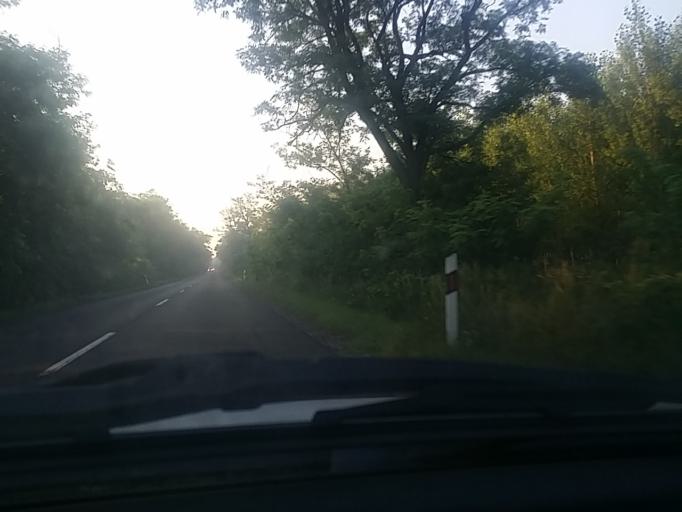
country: HU
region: Pest
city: Forropuszta
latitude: 47.4620
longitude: 19.6551
